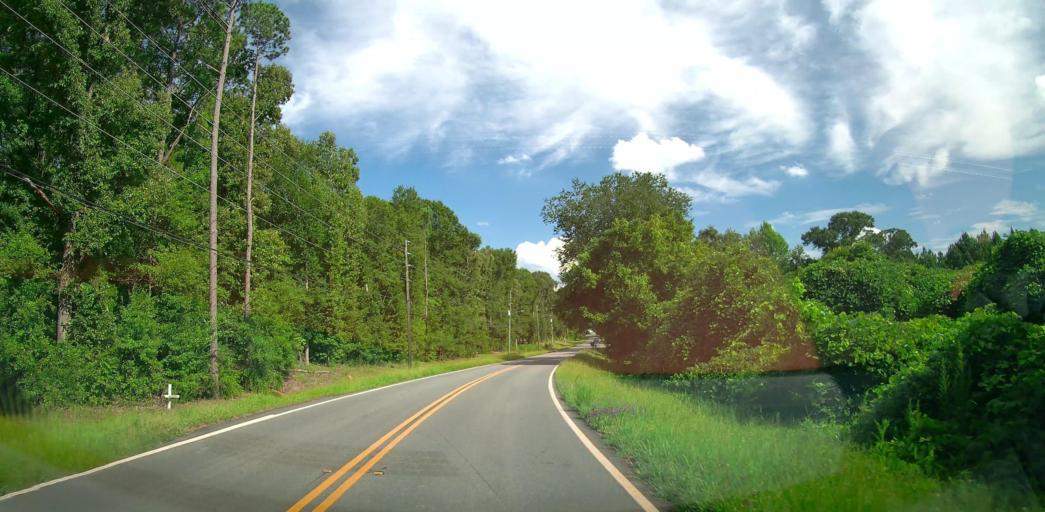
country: US
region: Georgia
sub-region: Houston County
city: Centerville
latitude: 32.5376
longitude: -83.6751
